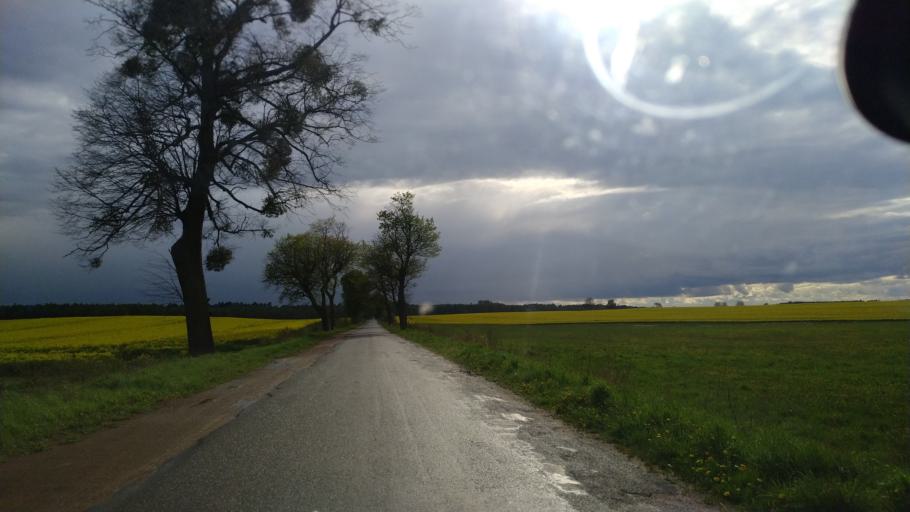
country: PL
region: Pomeranian Voivodeship
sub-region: Powiat starogardzki
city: Smetowo Graniczne
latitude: 53.7165
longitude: 18.6065
